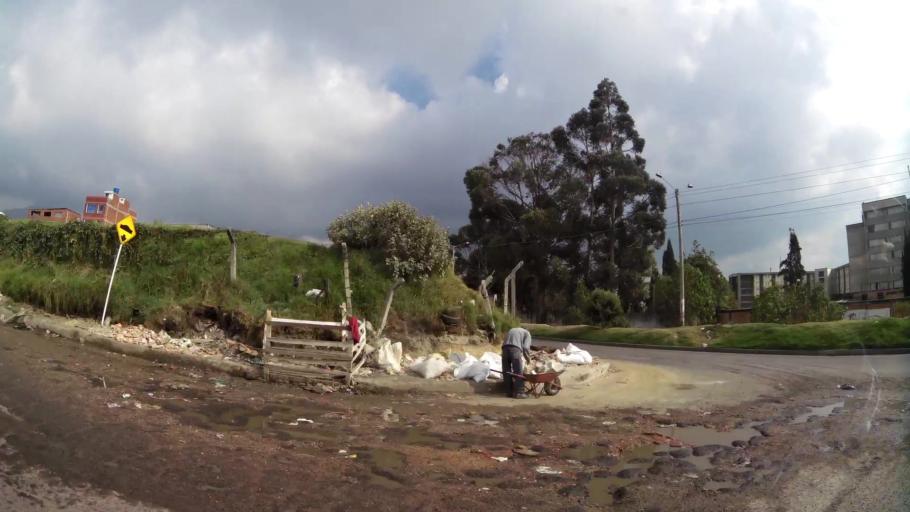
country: CO
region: Bogota D.C.
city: Bogota
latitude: 4.5519
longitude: -74.1179
